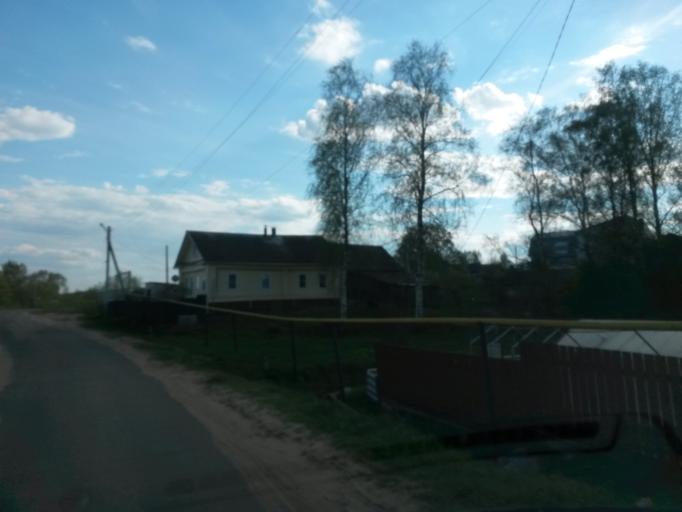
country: RU
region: Jaroslavl
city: Myshkin
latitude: 57.7822
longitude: 38.4485
